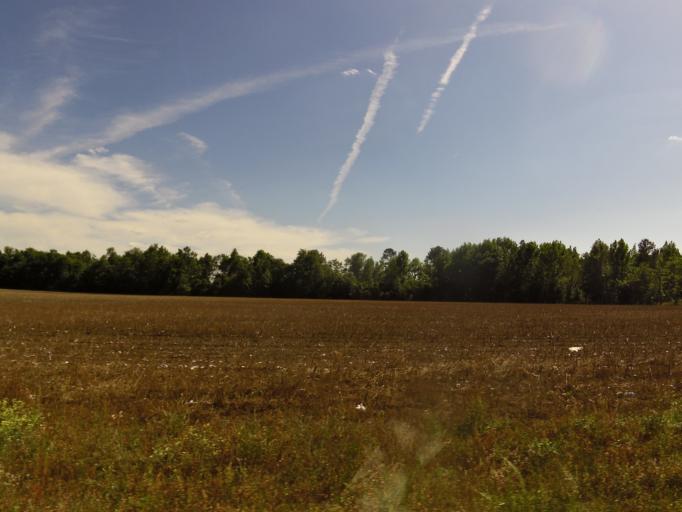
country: US
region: South Carolina
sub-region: Bamberg County
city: Denmark
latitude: 33.3364
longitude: -81.1665
